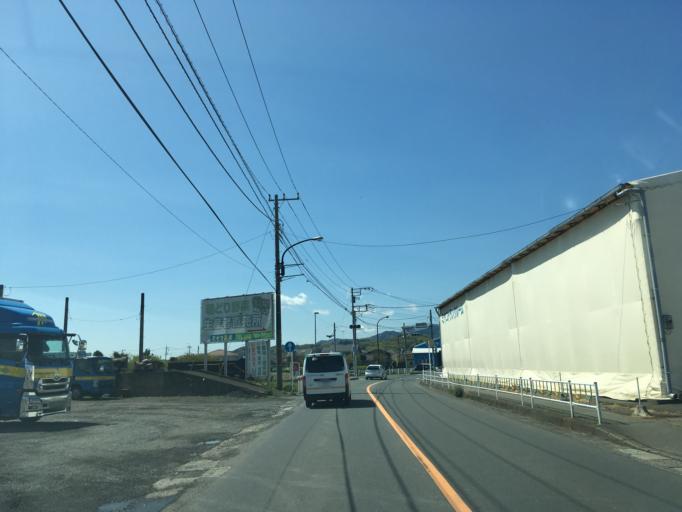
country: JP
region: Tokyo
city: Hachioji
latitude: 35.5723
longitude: 139.3237
